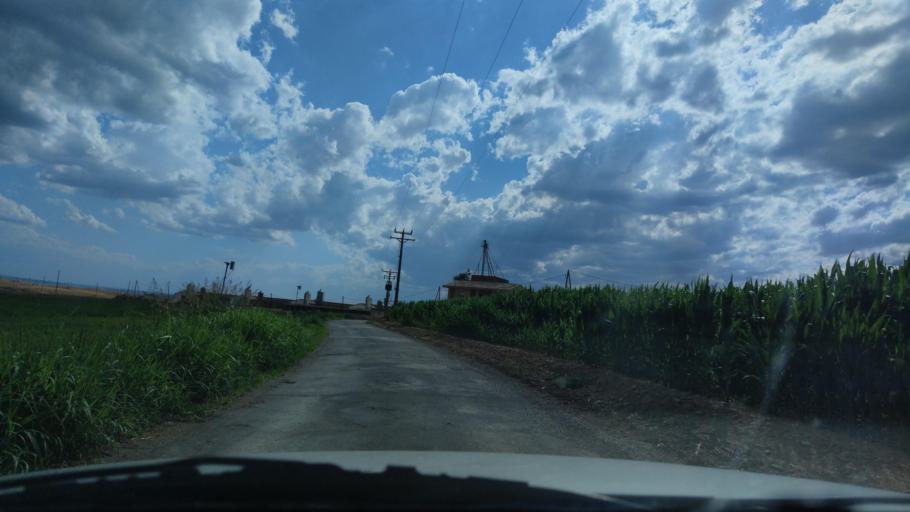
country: ES
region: Catalonia
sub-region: Provincia de Lleida
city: Alcarras
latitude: 41.6010
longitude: 0.5449
